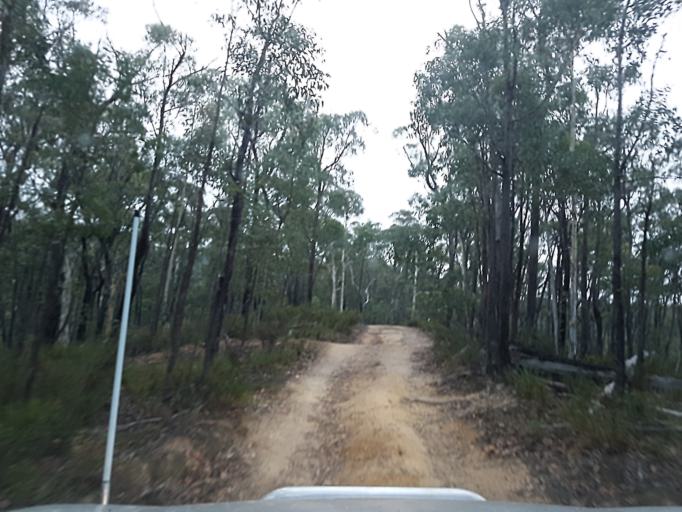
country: AU
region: New South Wales
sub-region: Snowy River
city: Jindabyne
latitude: -36.8587
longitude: 148.2334
